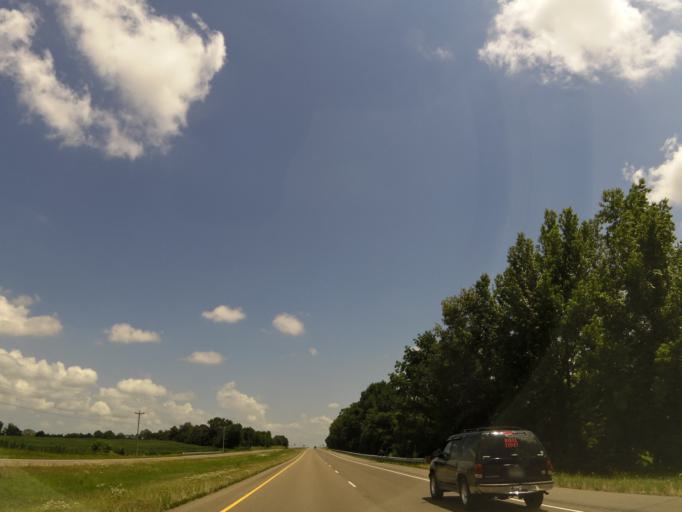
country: US
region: Tennessee
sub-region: Lauderdale County
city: Halls
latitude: 35.8970
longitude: -89.2441
